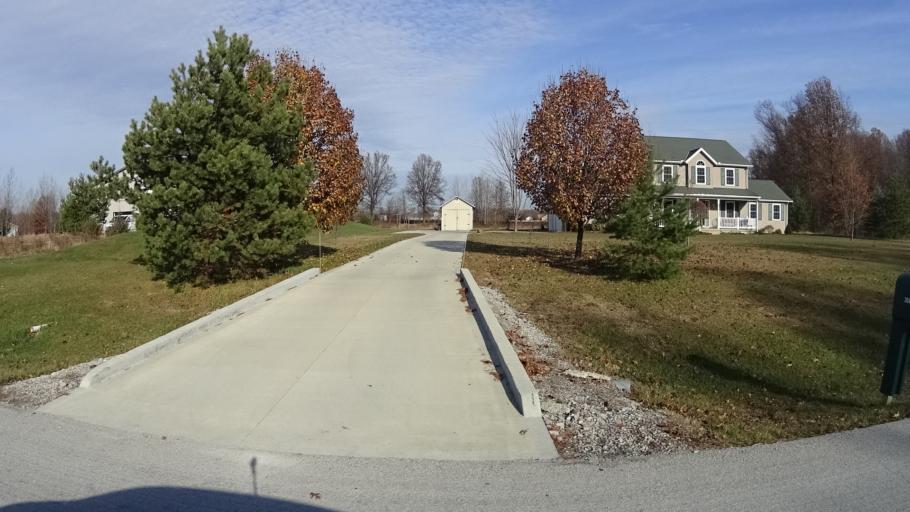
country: US
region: Ohio
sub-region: Lorain County
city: Grafton
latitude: 41.2184
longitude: -82.0402
